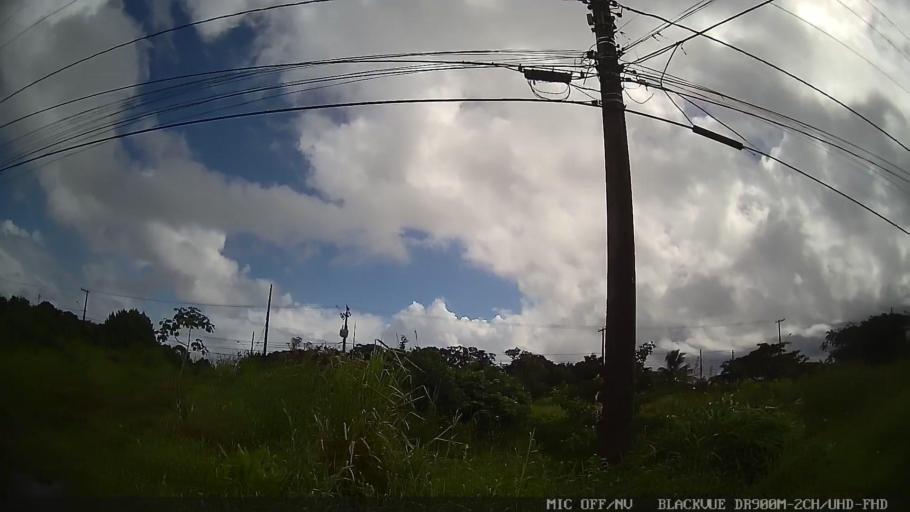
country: BR
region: Sao Paulo
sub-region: Itanhaem
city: Itanhaem
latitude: -24.2242
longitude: -46.8701
